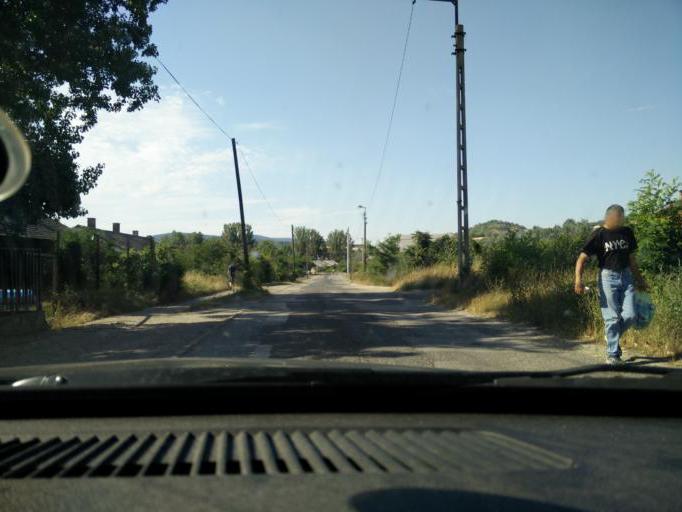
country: HU
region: Fejer
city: Szarliget
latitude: 47.5530
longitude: 18.4486
